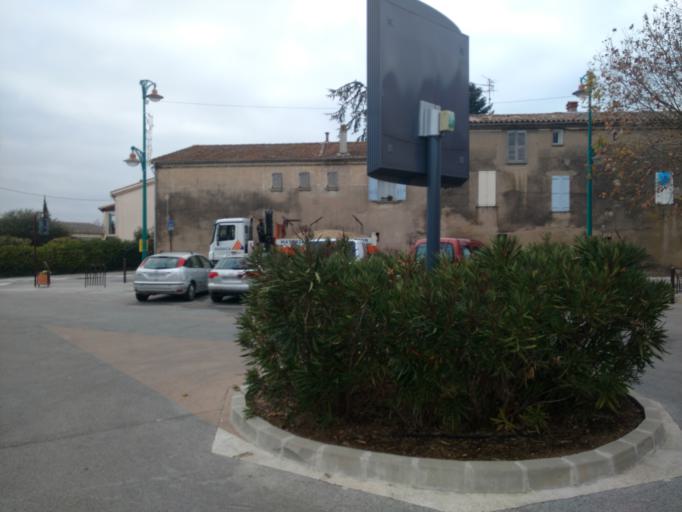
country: FR
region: Provence-Alpes-Cote d'Azur
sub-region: Departement du Var
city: Le Muy
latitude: 43.4735
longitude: 6.5631
